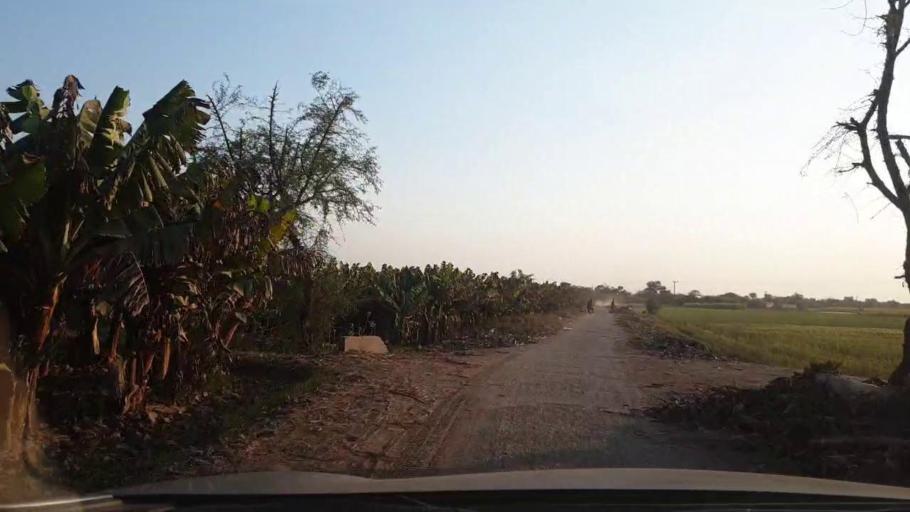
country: PK
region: Sindh
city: Tando Adam
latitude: 25.6766
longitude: 68.7431
